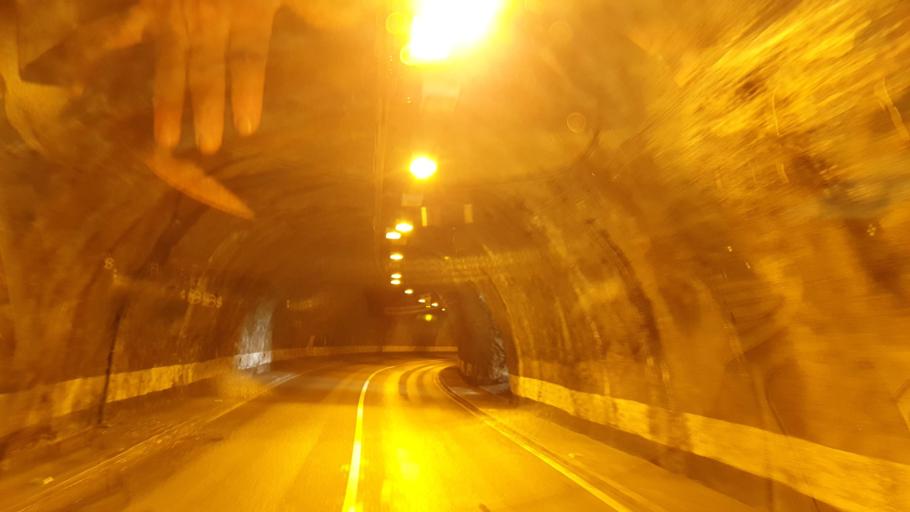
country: AT
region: Vorarlberg
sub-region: Politischer Bezirk Bregenz
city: Kennelbach
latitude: 47.4996
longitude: 9.7948
